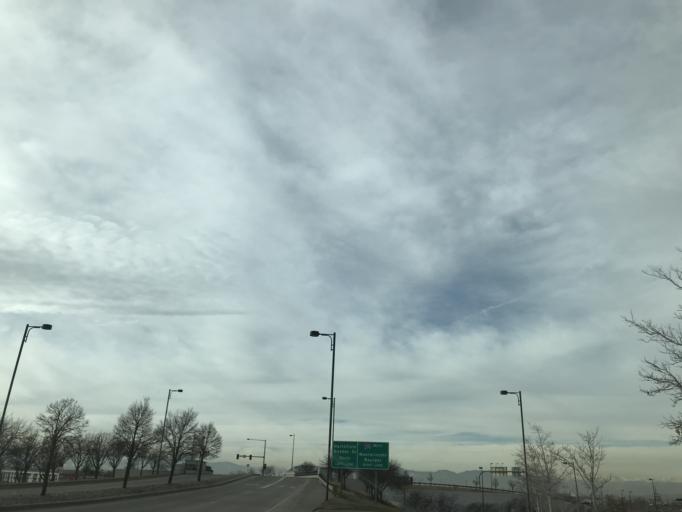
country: US
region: Colorado
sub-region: Adams County
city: Commerce City
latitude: 39.7819
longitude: -104.8990
